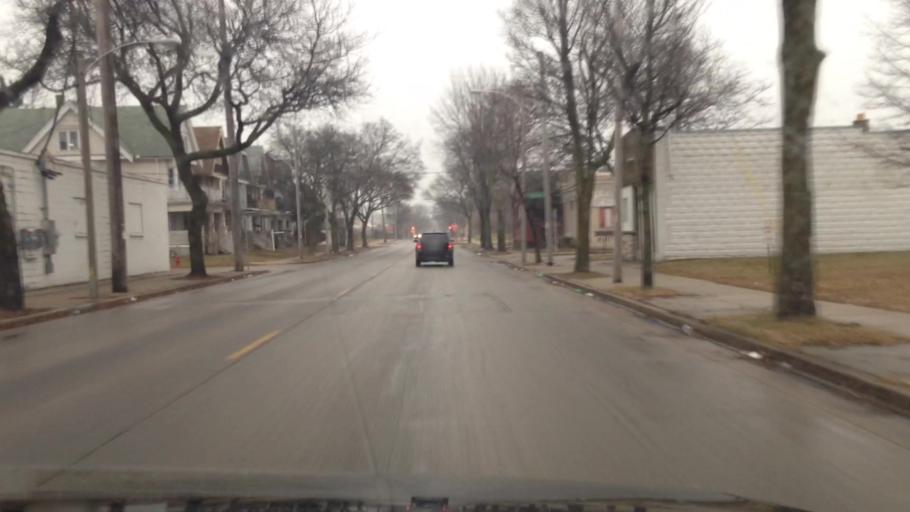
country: US
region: Wisconsin
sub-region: Milwaukee County
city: Shorewood
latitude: 43.0821
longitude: -87.9094
